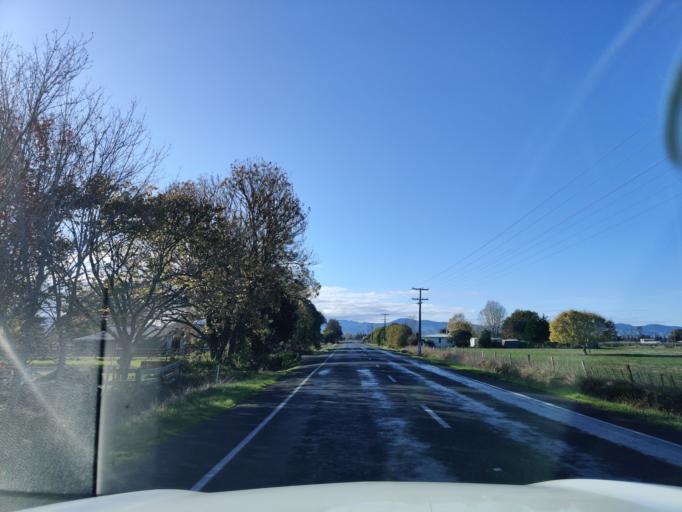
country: NZ
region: Waikato
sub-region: Hauraki District
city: Ngatea
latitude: -37.3113
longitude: 175.5760
